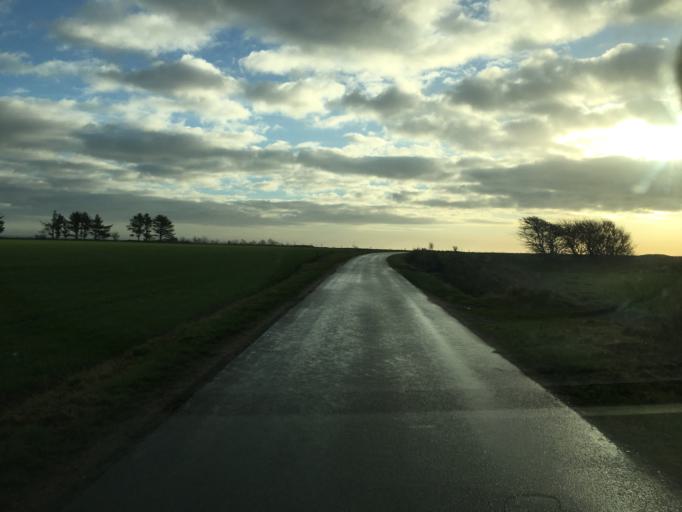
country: DK
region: South Denmark
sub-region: Tonder Kommune
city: Sherrebek
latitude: 55.1631
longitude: 8.8141
